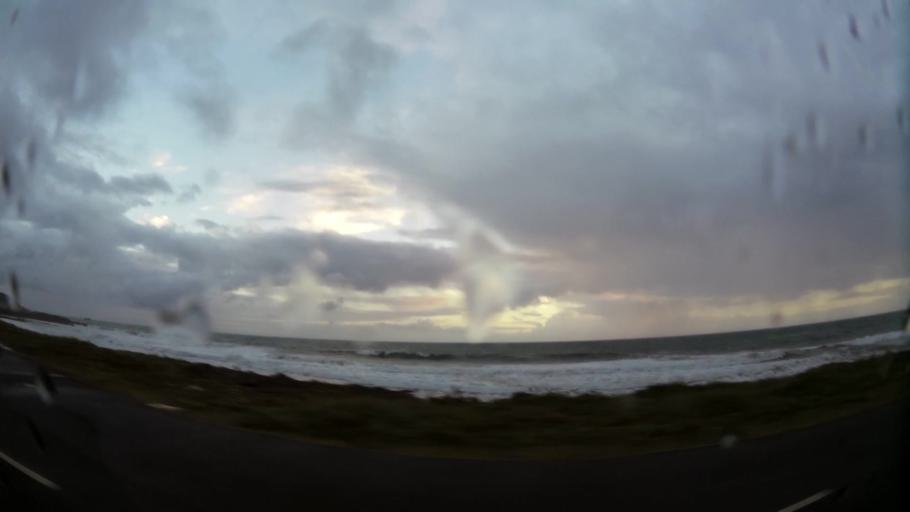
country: DM
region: Saint Andrew
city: Marigot
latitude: 15.5455
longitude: -61.2909
